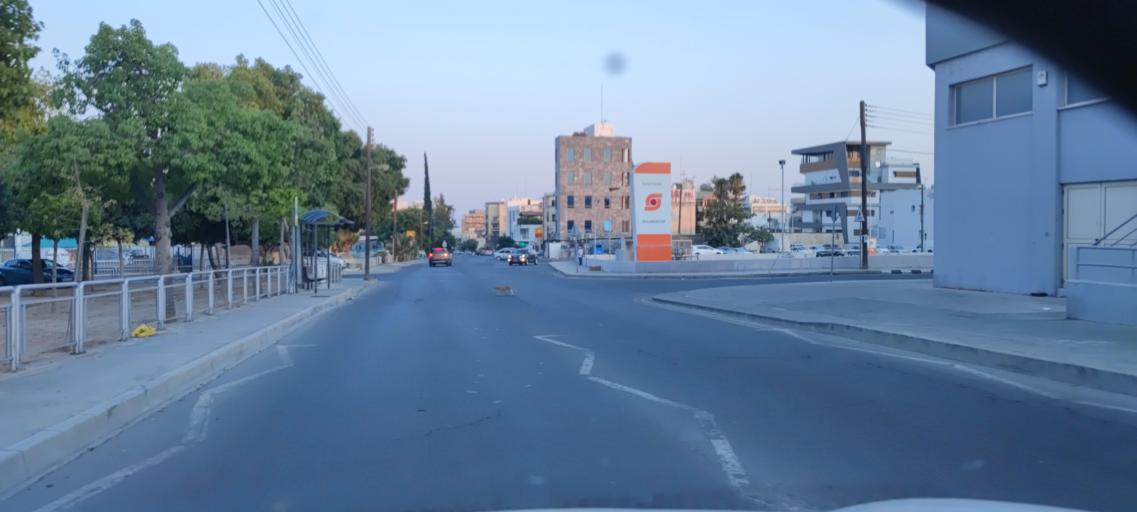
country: CY
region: Limassol
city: Limassol
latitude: 34.6921
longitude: 33.0529
